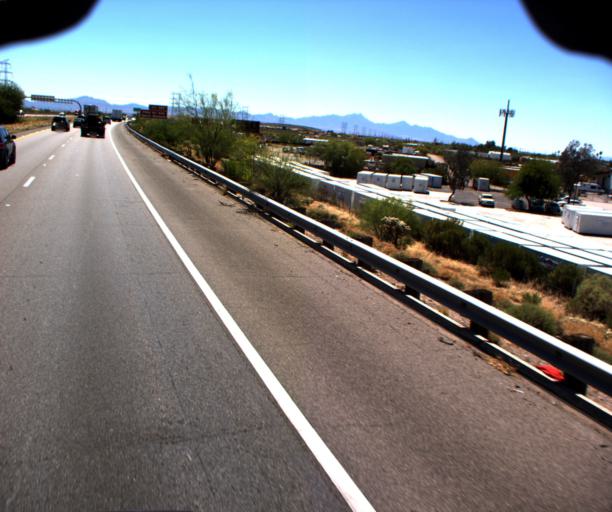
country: US
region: Arizona
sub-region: Pima County
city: Tucson
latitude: 32.1461
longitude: -110.8940
